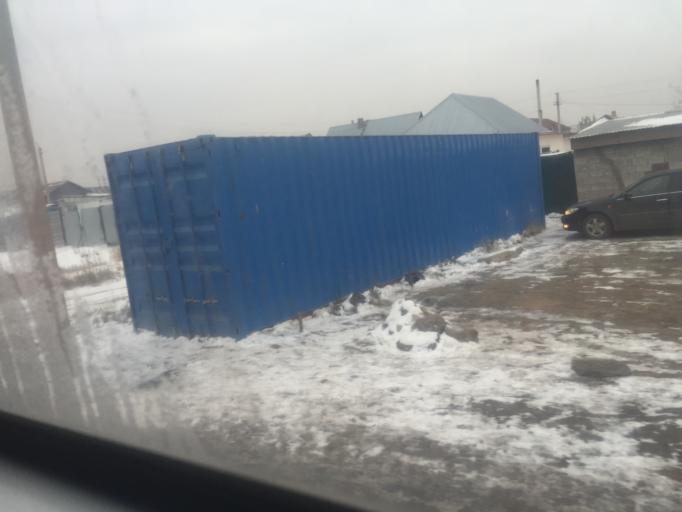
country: KZ
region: Astana Qalasy
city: Astana
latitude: 51.2083
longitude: 71.4062
